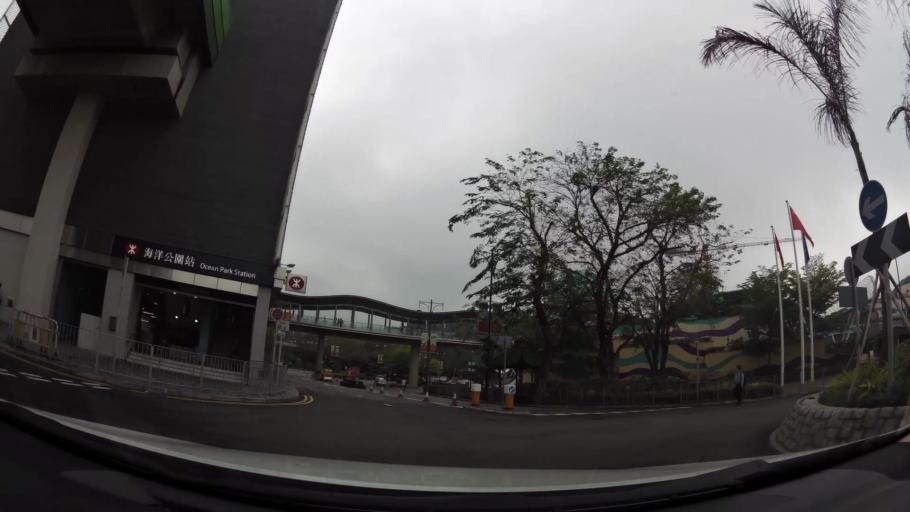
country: HK
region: Wanchai
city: Wan Chai
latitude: 22.2483
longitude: 114.1738
